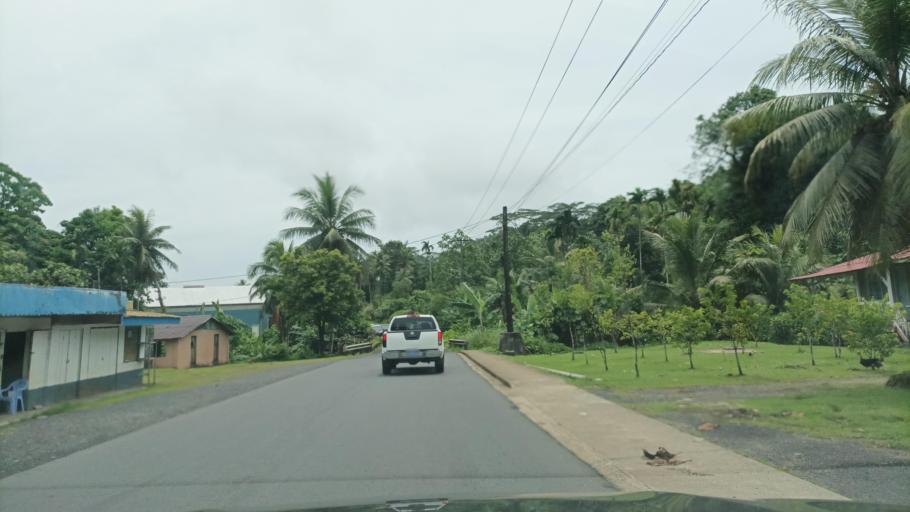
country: FM
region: Pohnpei
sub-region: Sokehs Municipality
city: Palikir - National Government Center
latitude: 6.9382
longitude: 158.1840
